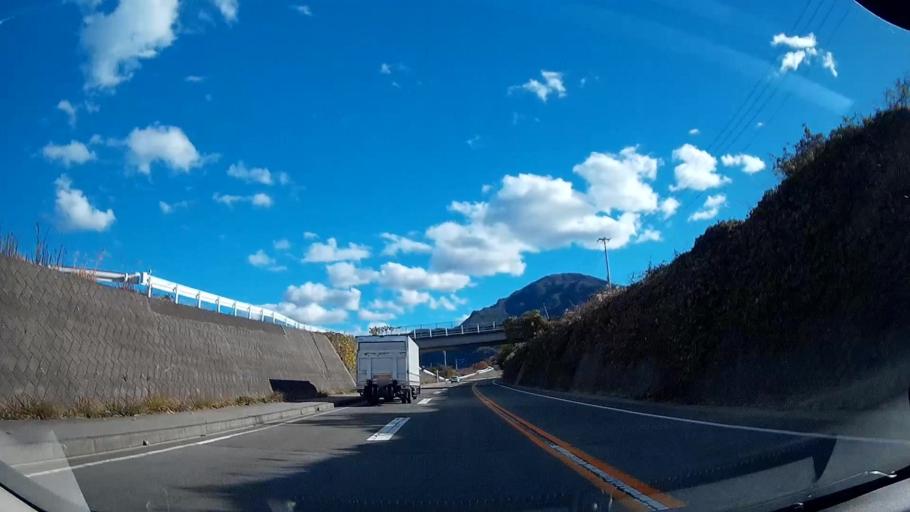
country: JP
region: Yamanashi
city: Isawa
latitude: 35.6030
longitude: 138.7060
